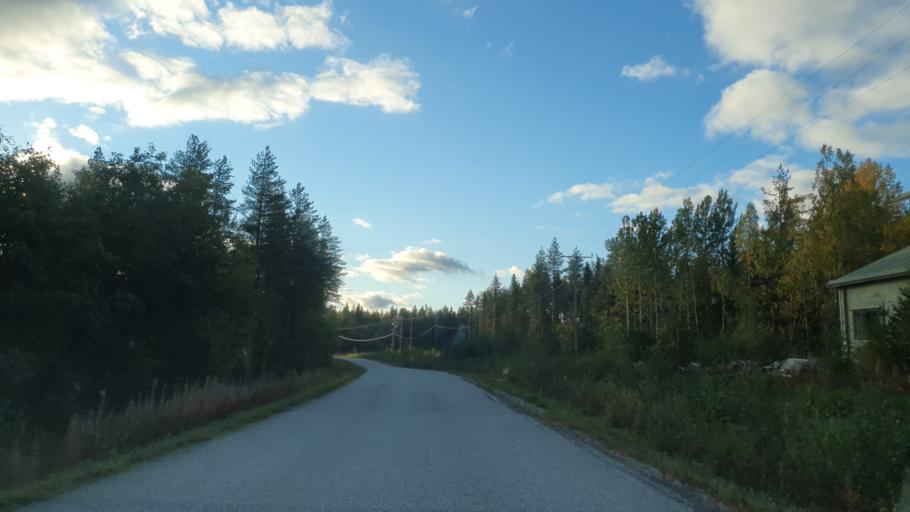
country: FI
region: Kainuu
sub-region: Kehys-Kainuu
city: Kuhmo
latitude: 63.9544
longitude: 29.7354
